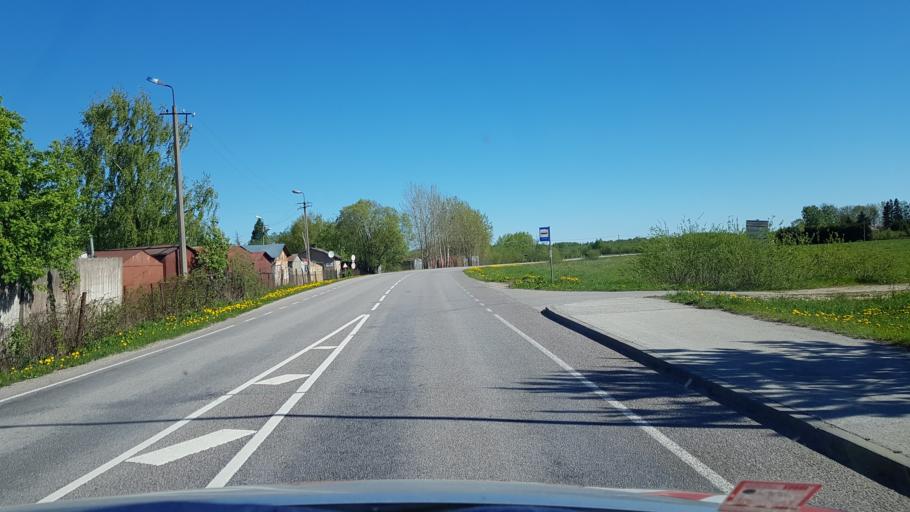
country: EE
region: Tartu
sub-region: Tartu linn
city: Tartu
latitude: 58.3821
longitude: 26.7792
